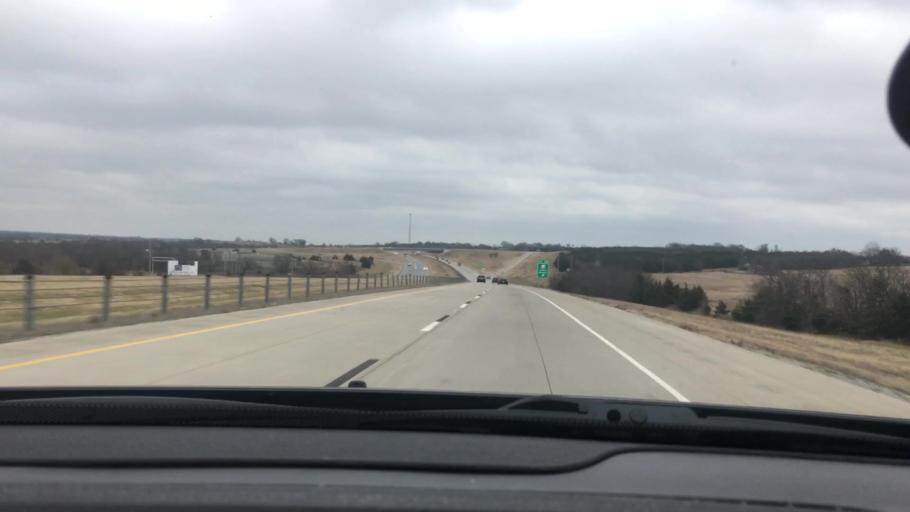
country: US
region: Oklahoma
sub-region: Bryan County
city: Durant
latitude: 34.1251
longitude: -96.2819
